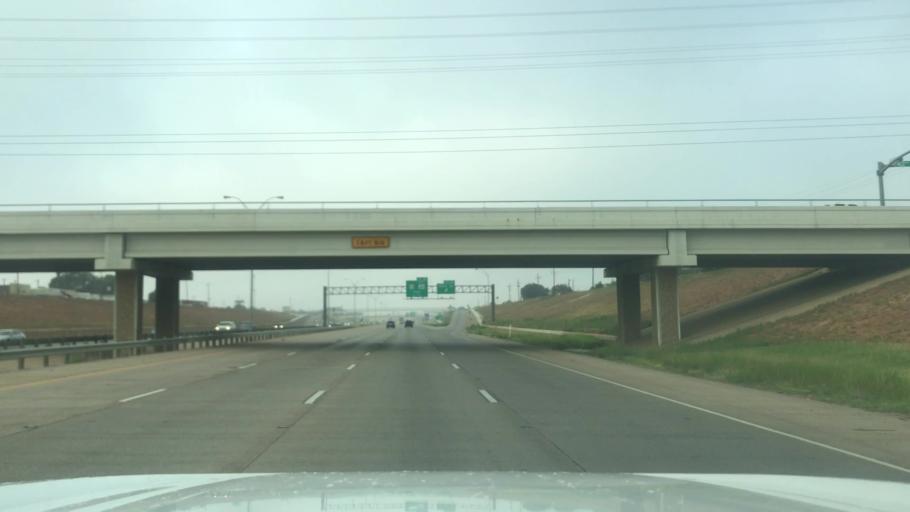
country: US
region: Texas
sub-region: Lubbock County
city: Lubbock
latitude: 33.5566
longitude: -101.8452
